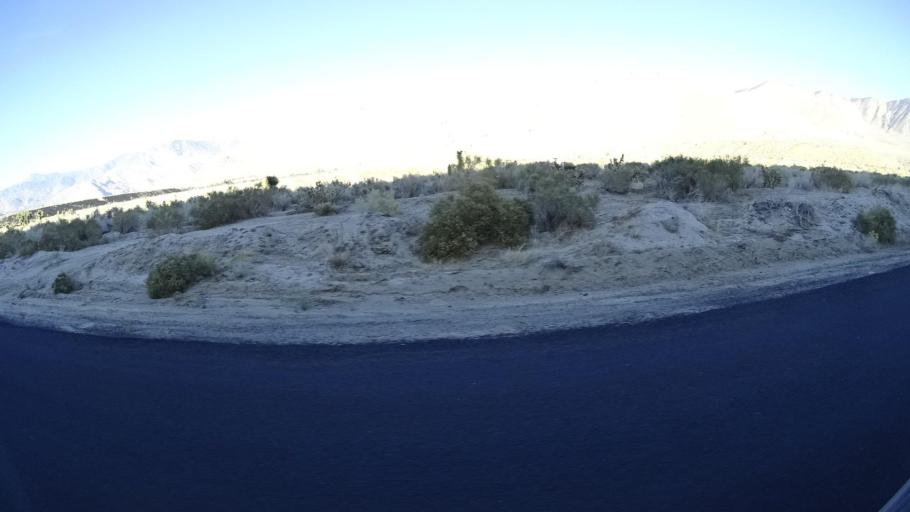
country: US
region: California
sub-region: Kern County
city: Weldon
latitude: 35.6152
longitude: -118.2496
